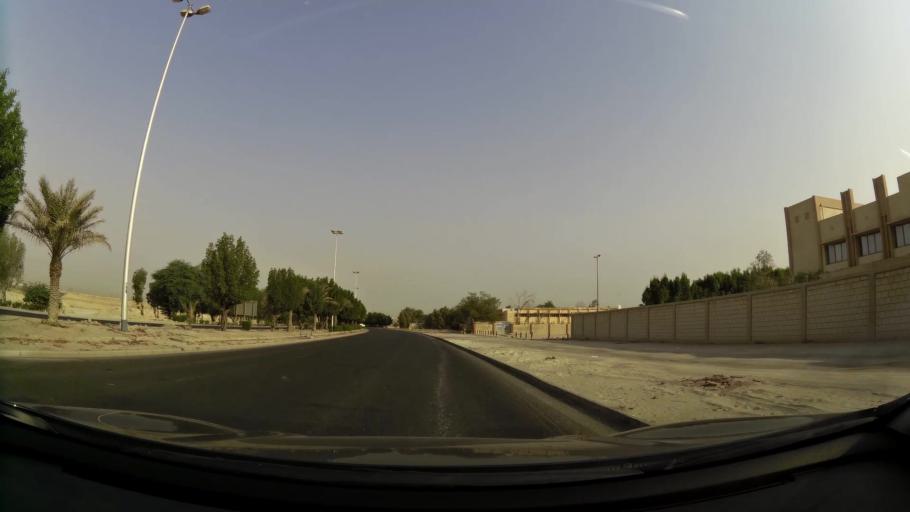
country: KW
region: Al Asimah
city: Ar Rabiyah
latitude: 29.3137
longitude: 47.8063
